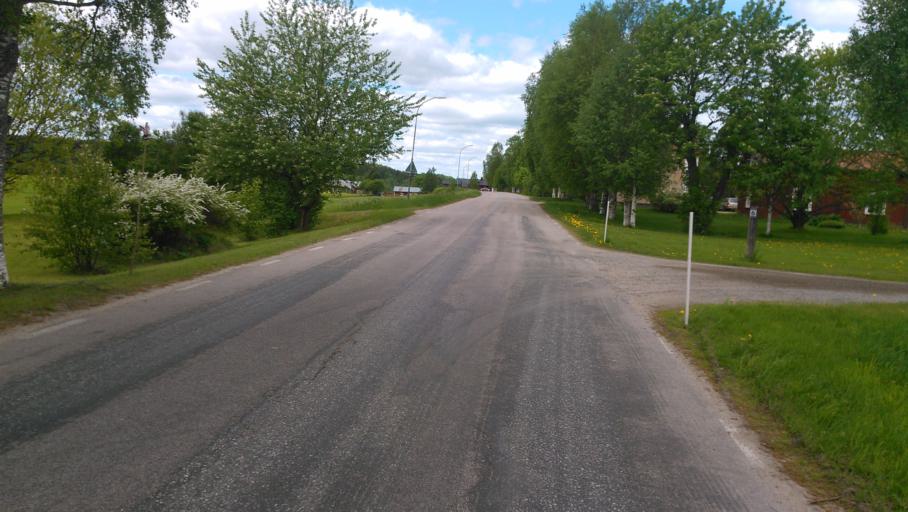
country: SE
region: Vaesterbotten
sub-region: Umea Kommun
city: Roback
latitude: 63.8642
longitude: 20.0830
